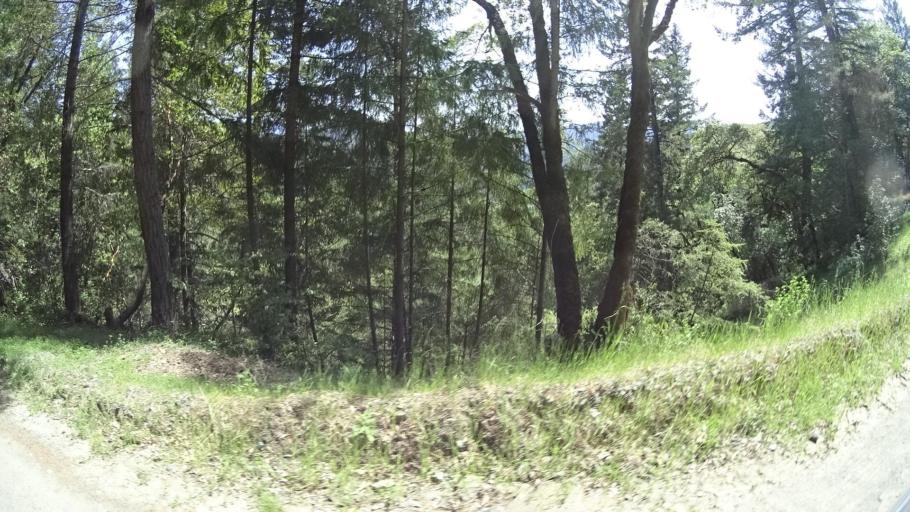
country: US
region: California
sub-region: Humboldt County
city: Redway
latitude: 40.2119
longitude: -123.6589
